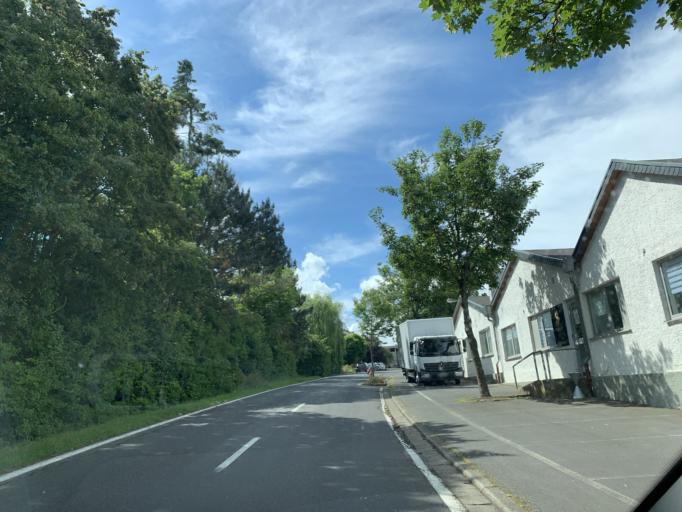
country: DE
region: Rheinland-Pfalz
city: Mastershausen
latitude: 50.0678
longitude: 7.3574
